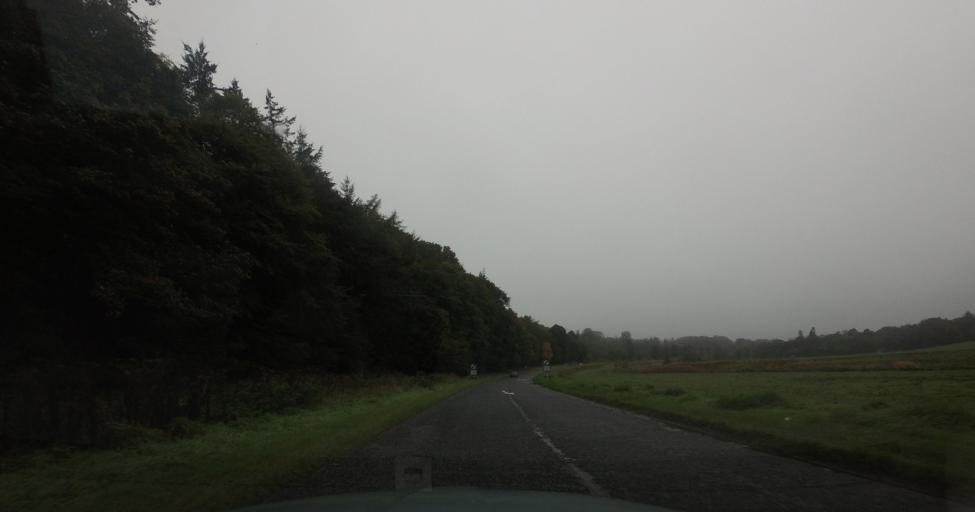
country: GB
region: Scotland
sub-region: Aberdeenshire
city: Oldmeldrum
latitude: 57.4293
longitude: -2.3996
